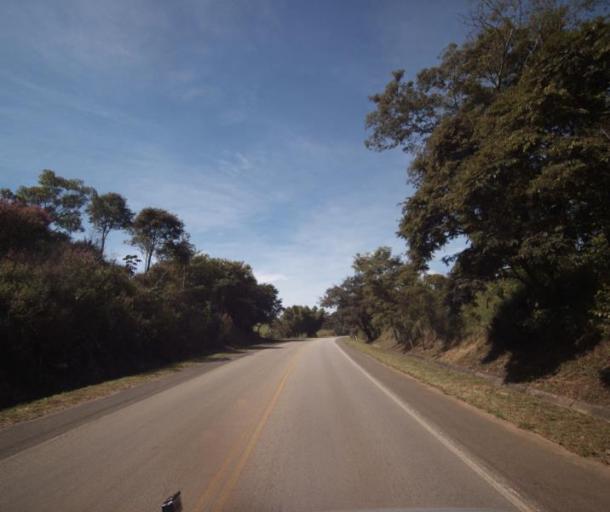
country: BR
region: Goias
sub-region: Abadiania
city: Abadiania
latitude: -16.1313
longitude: -48.8936
